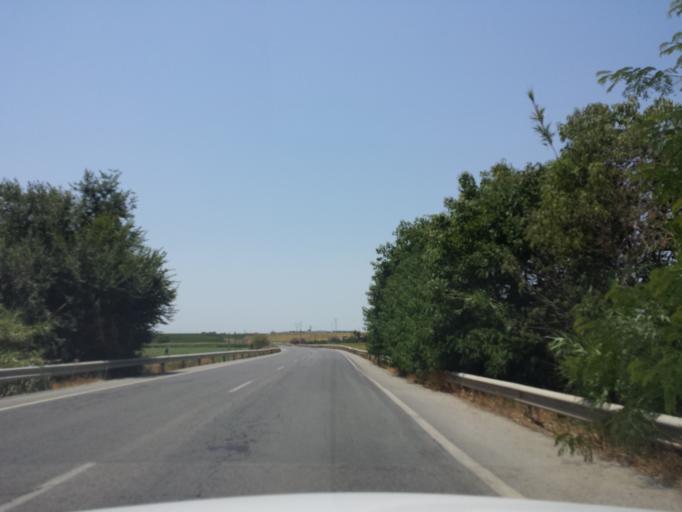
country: ES
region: Andalusia
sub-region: Provincia de Sevilla
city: Acala del Rio
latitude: 37.5407
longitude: -5.9484
